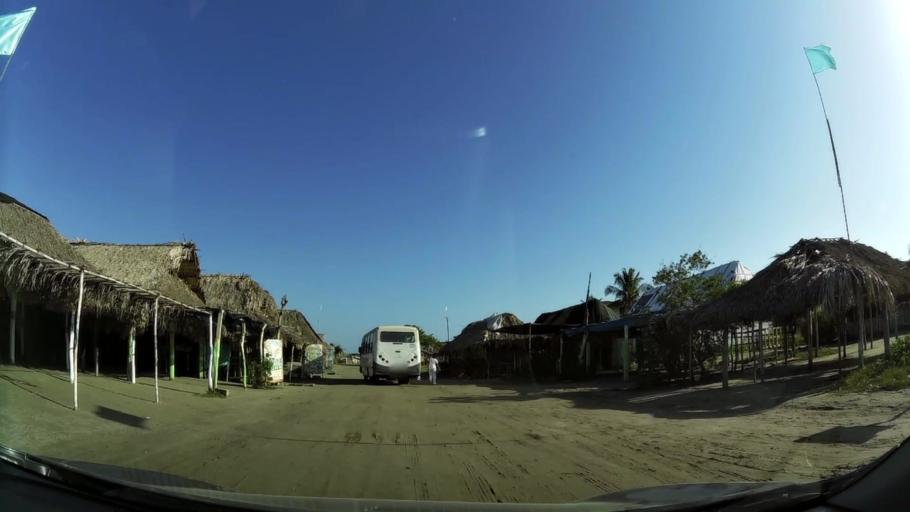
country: CO
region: Bolivar
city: Cartagena
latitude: 10.4850
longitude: -75.4922
